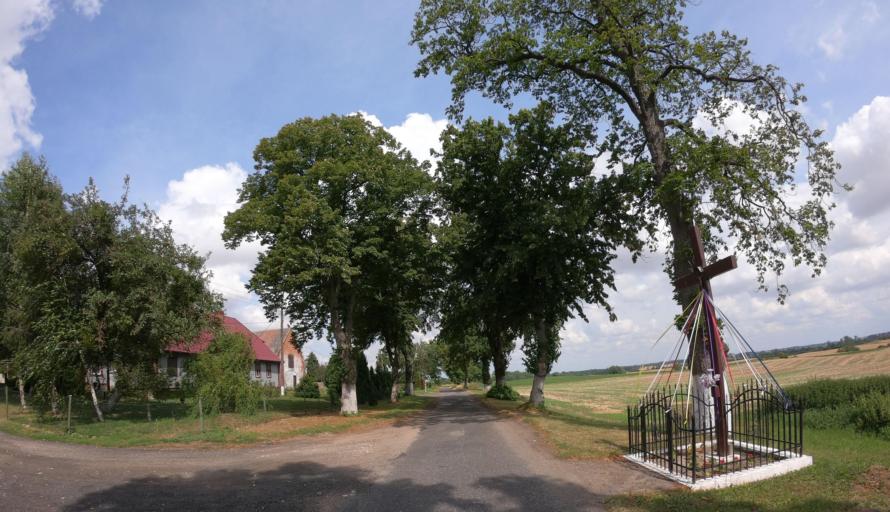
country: PL
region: West Pomeranian Voivodeship
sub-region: Powiat pyrzycki
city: Kozielice
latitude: 53.0548
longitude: 14.8927
